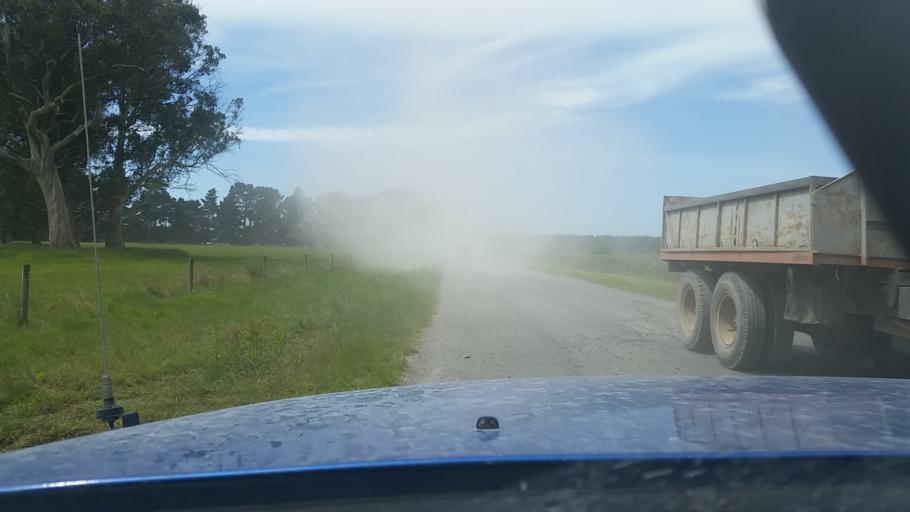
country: NZ
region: Canterbury
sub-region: Ashburton District
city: Tinwald
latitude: -44.0907
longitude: 171.6869
